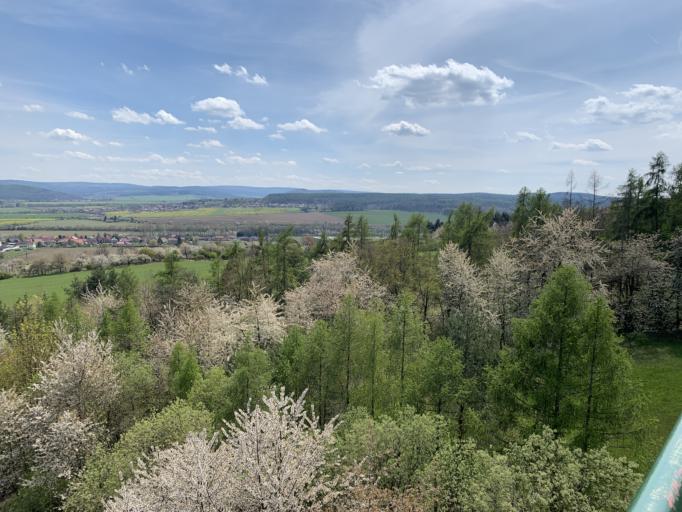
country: CZ
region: Plzensky
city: Zbiroh
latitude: 49.8545
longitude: 13.8231
